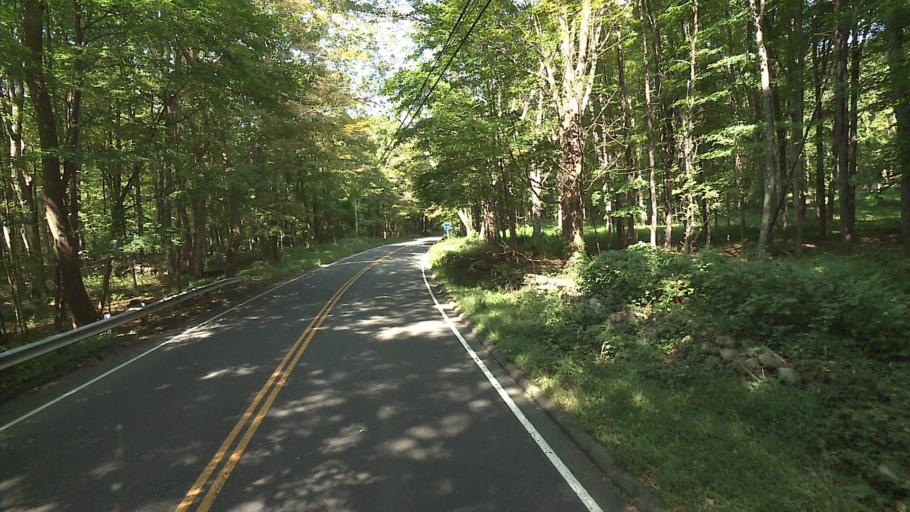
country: US
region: Connecticut
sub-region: Fairfield County
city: Georgetown
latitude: 41.2814
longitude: -73.3412
